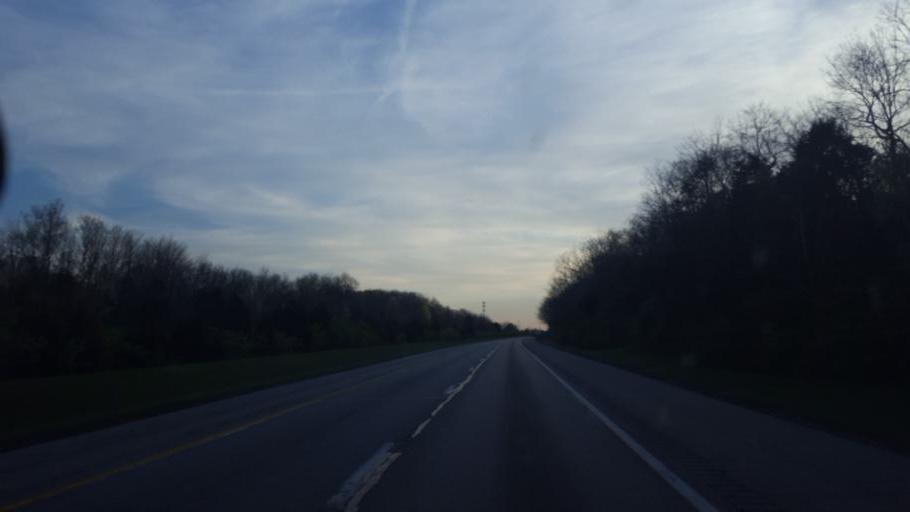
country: US
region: Ohio
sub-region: Warren County
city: South Lebanon
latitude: 39.3890
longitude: -84.2050
